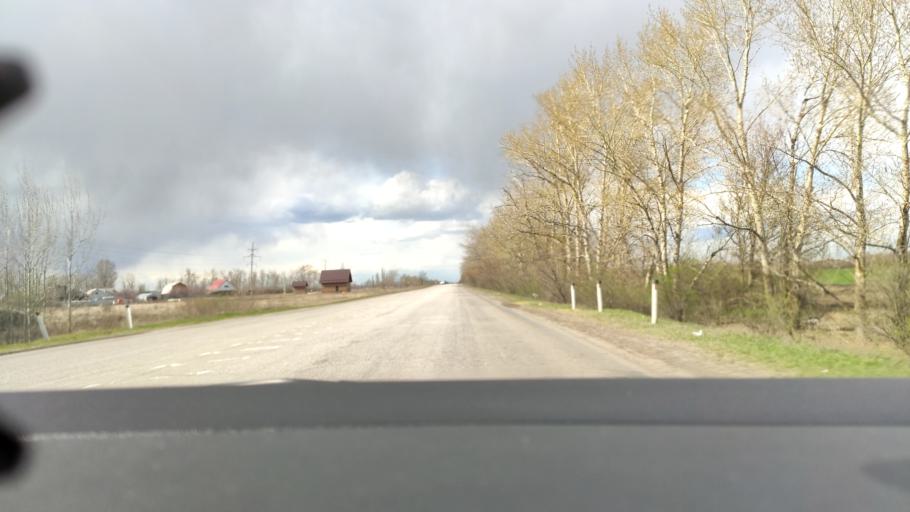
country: RU
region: Voronezj
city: Maslovka
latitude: 51.5121
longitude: 39.3035
